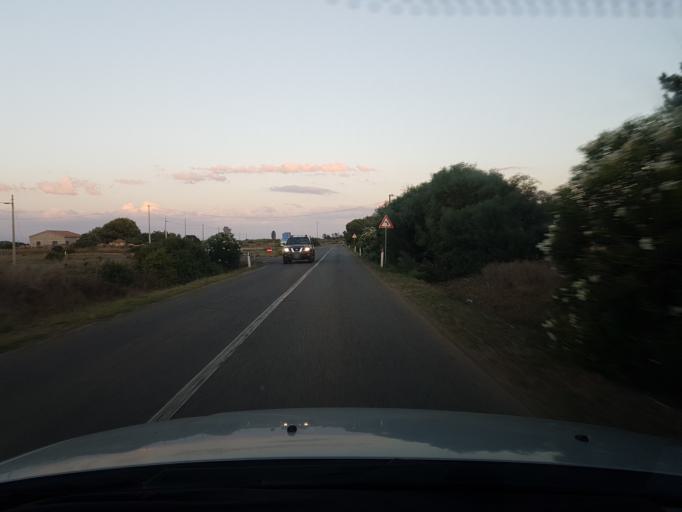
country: IT
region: Sardinia
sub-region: Provincia di Oristano
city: Riola Sardo
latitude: 40.0265
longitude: 8.4287
